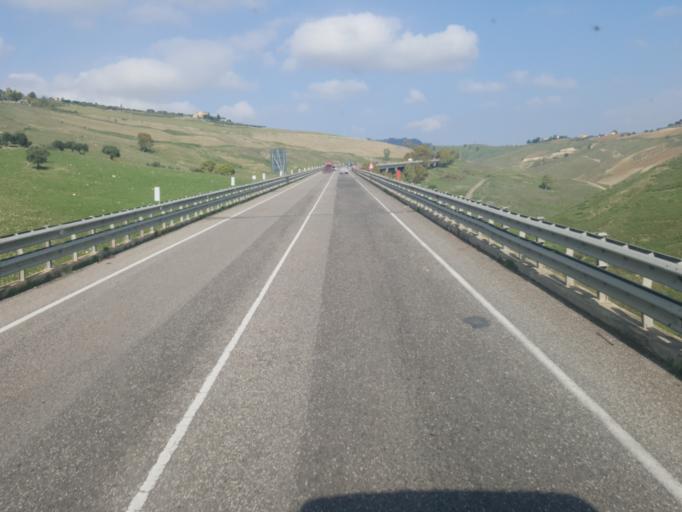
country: IT
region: Sicily
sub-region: Enna
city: Pietraperzia
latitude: 37.4624
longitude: 14.1024
